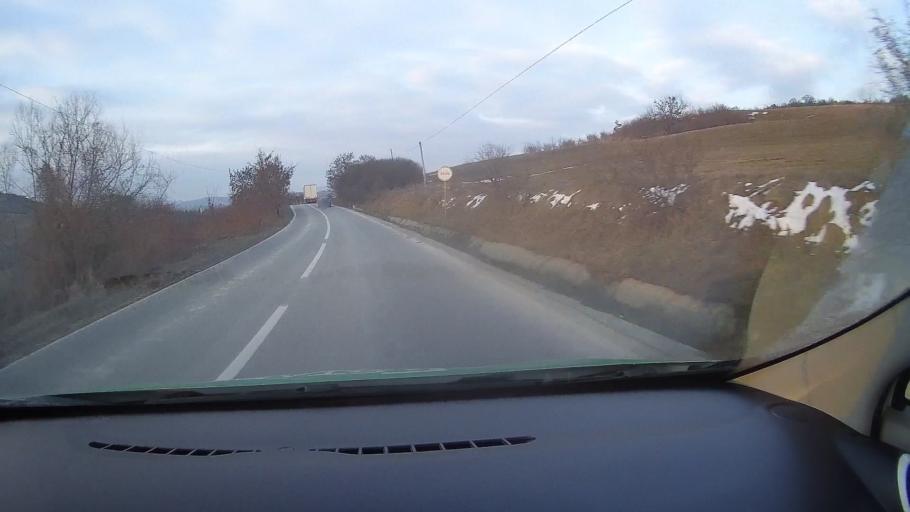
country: RO
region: Harghita
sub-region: Comuna Simonesti
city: Simonesti
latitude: 46.3249
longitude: 25.1017
